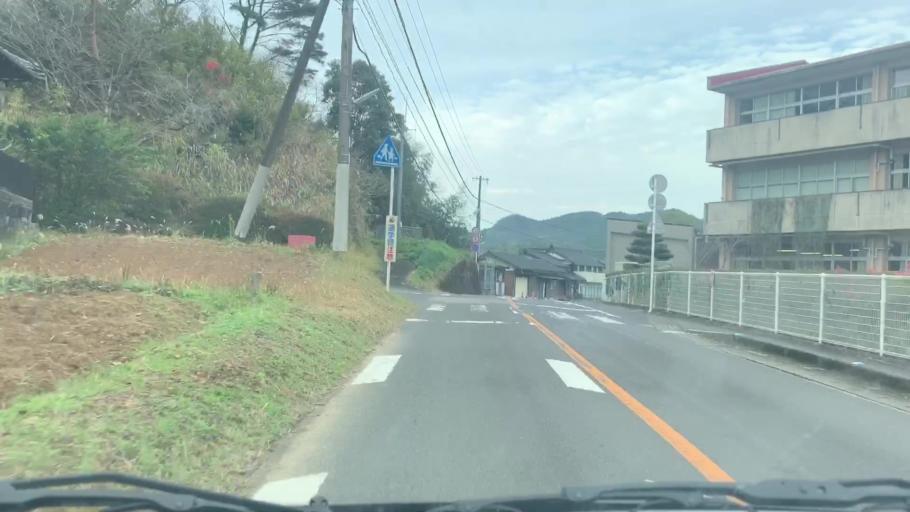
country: JP
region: Saga Prefecture
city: Takeocho-takeo
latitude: 33.1929
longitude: 129.9643
